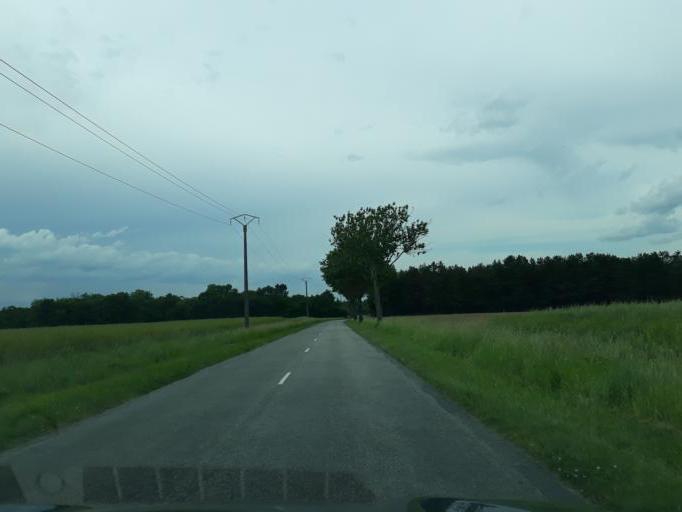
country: FR
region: Centre
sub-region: Departement du Loiret
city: Jargeau
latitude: 47.8497
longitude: 2.1342
